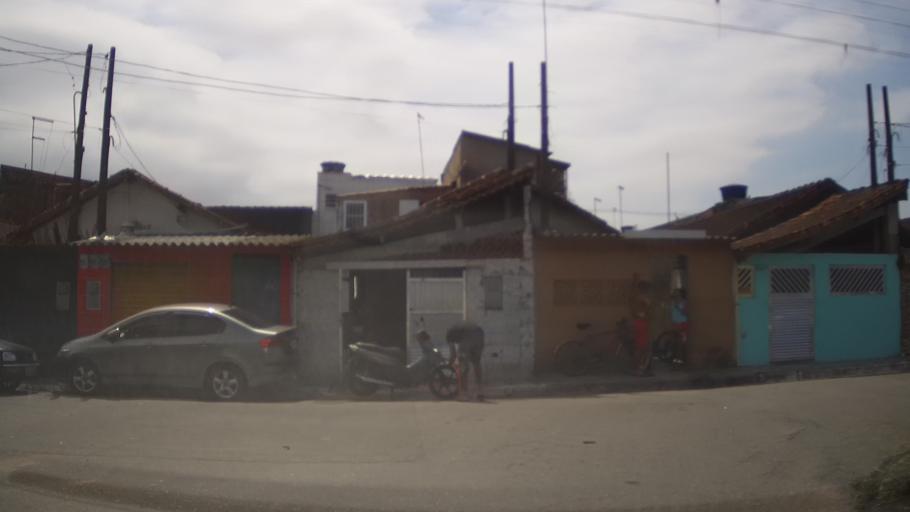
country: BR
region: Sao Paulo
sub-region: Praia Grande
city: Praia Grande
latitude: -24.0196
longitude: -46.4873
